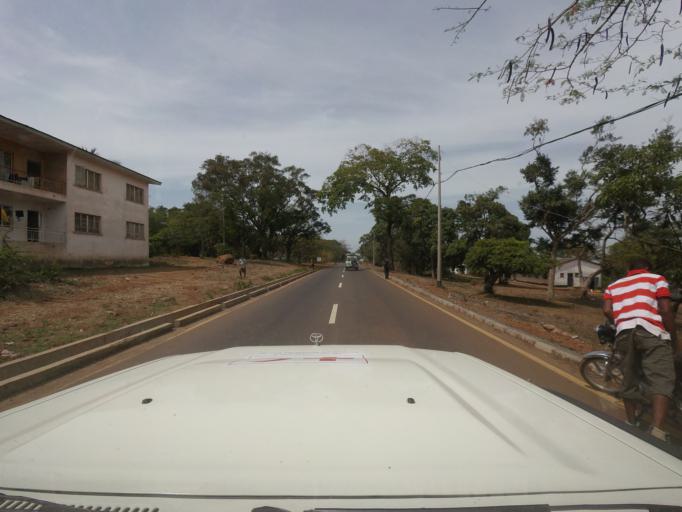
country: SL
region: Western Area
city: Freetown
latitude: 8.4662
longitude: -13.2164
